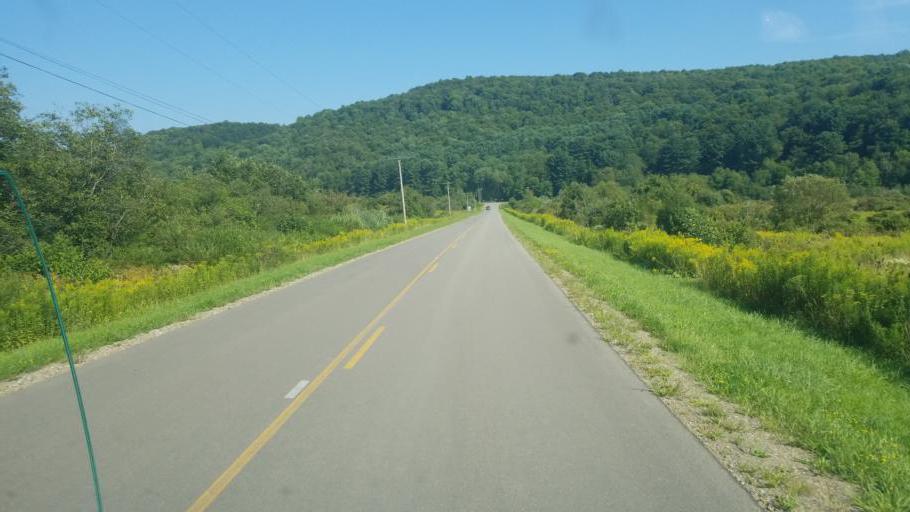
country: US
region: New York
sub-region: Allegany County
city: Wellsville
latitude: 42.0243
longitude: -77.9533
